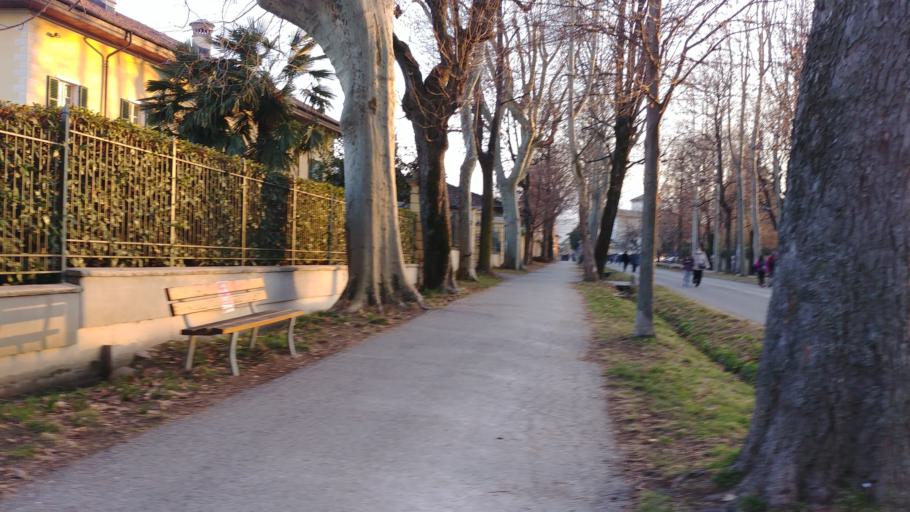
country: IT
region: Piedmont
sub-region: Provincia di Cuneo
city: Cuneo
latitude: 44.3683
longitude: 7.5384
